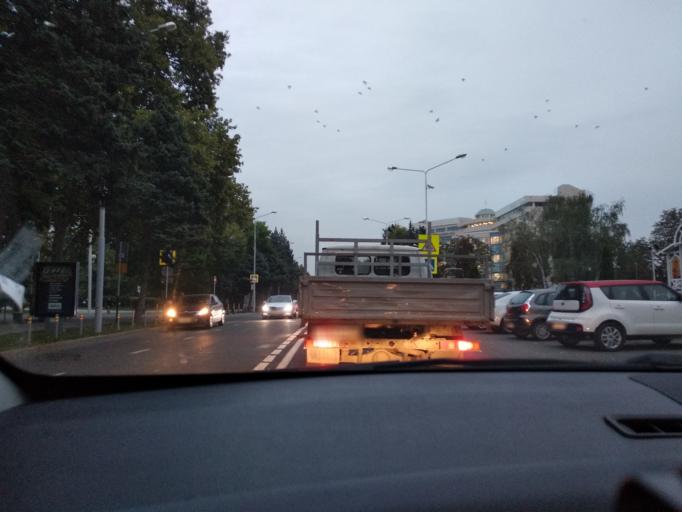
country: RU
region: Krasnodarskiy
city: Krasnodar
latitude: 45.0149
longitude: 38.9666
